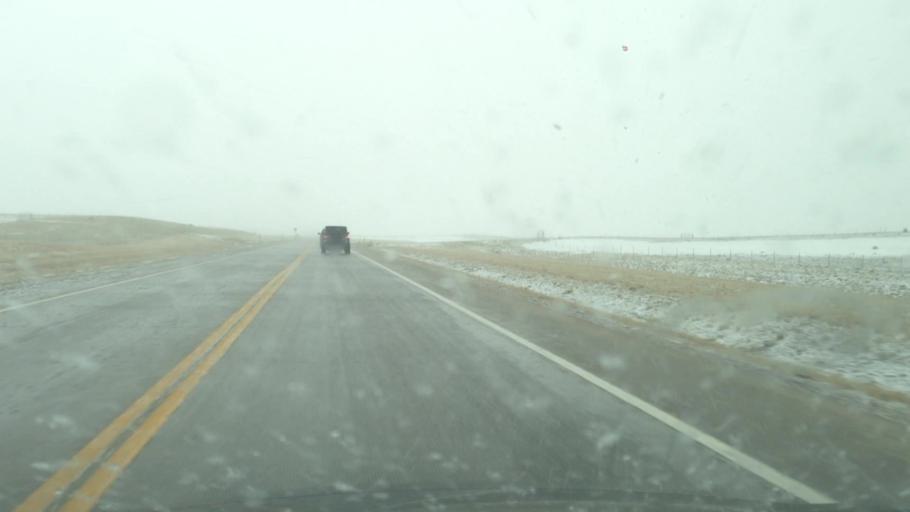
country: US
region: Colorado
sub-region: Park County
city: Castle Pines North
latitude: 39.4849
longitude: -104.8549
